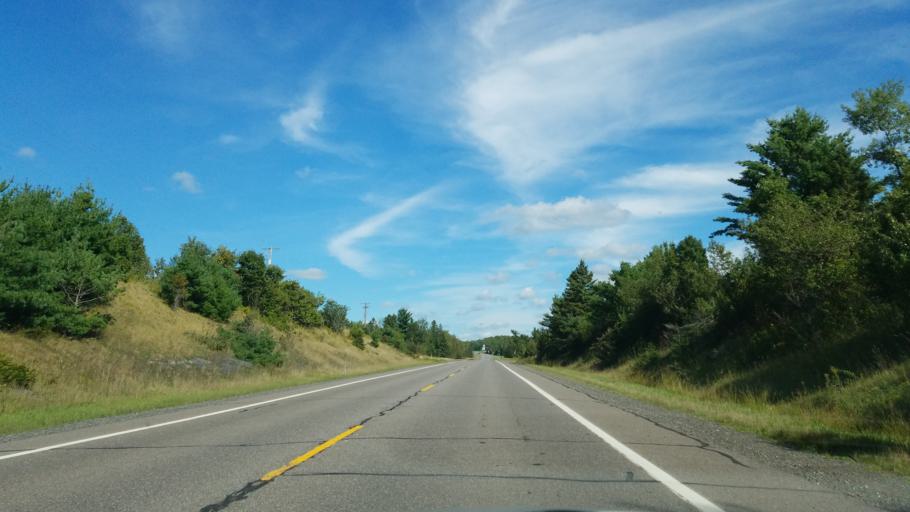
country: US
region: Michigan
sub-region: Baraga County
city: L'Anse
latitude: 46.5453
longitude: -88.5536
